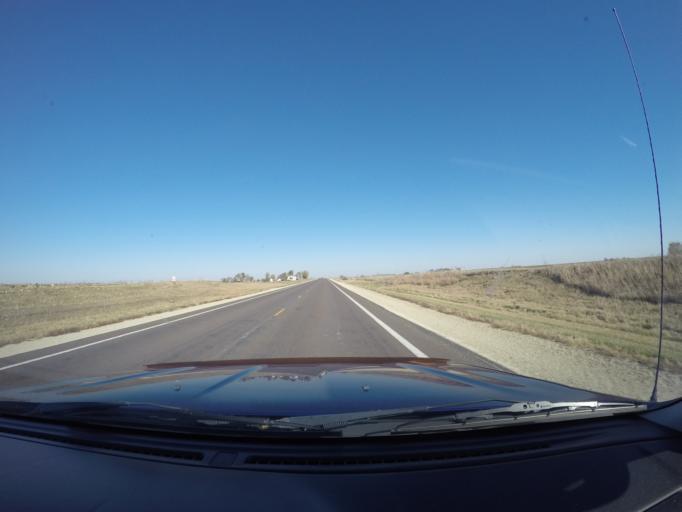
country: US
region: Kansas
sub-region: Marshall County
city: Blue Rapids
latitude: 39.6314
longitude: -96.7503
